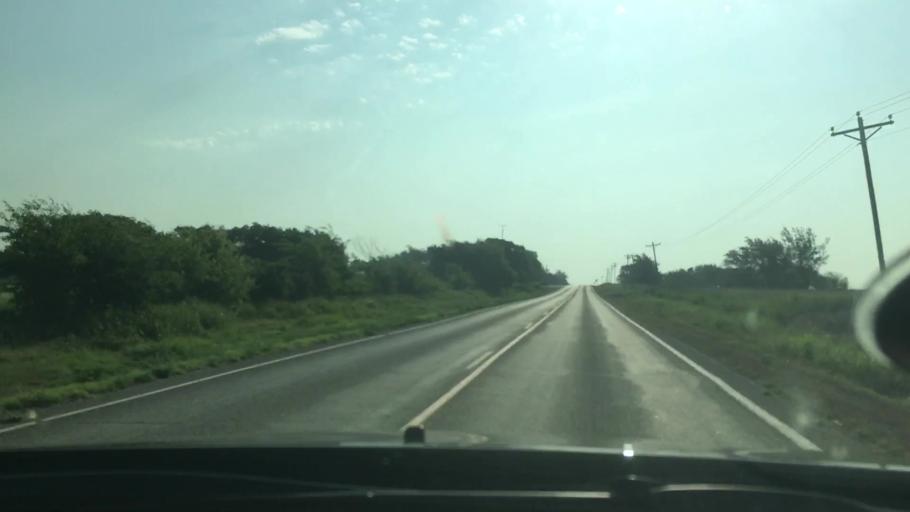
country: US
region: Oklahoma
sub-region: Bryan County
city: Durant
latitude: 34.1428
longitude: -96.3661
